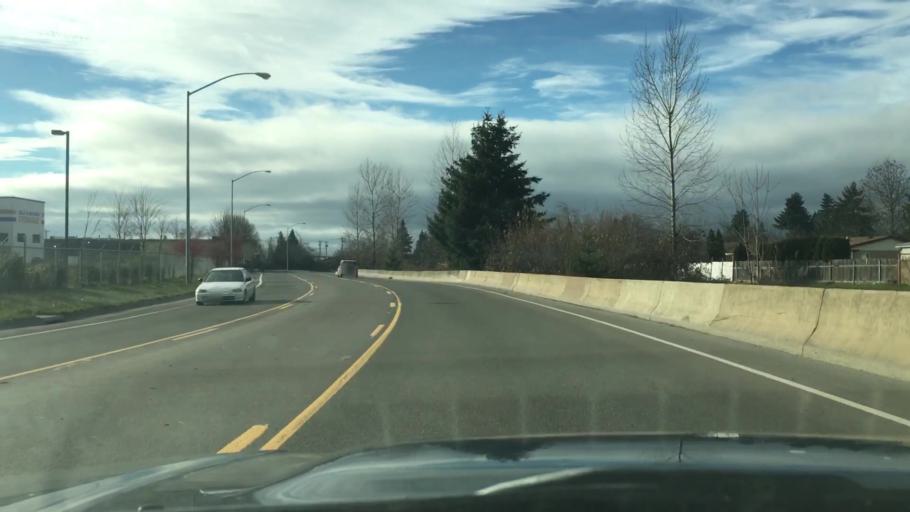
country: US
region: Oregon
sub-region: Lane County
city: Eugene
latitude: 44.0638
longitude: -123.1473
